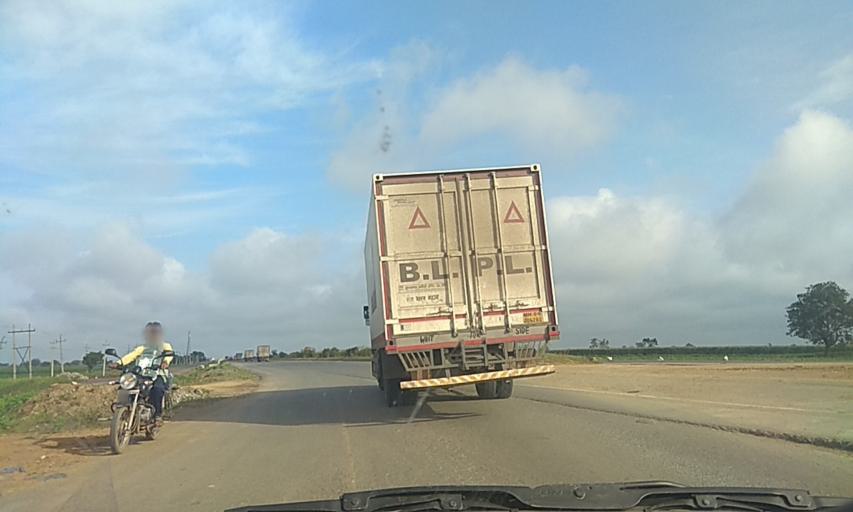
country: IN
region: Karnataka
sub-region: Haveri
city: Savanur
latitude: 14.8735
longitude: 75.3169
